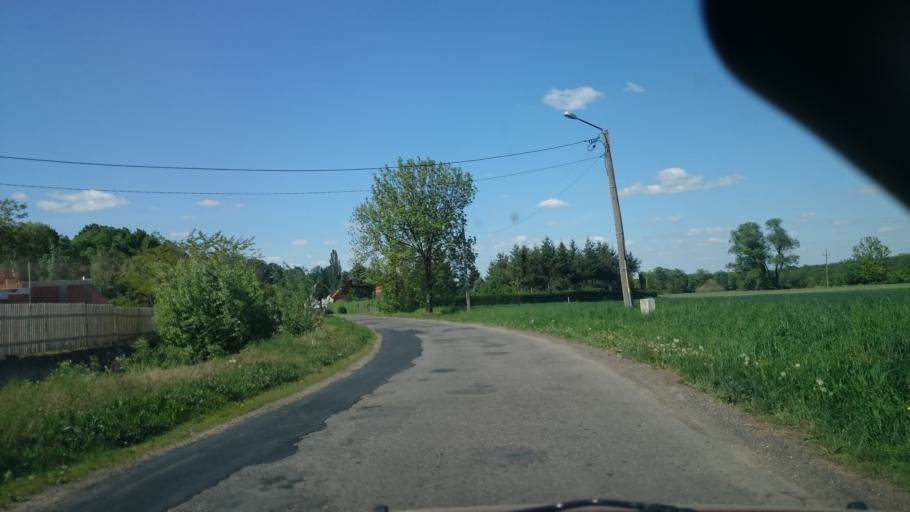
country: PL
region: Lower Silesian Voivodeship
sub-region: Powiat zabkowicki
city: Zloty Stok
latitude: 50.4680
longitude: 16.8467
